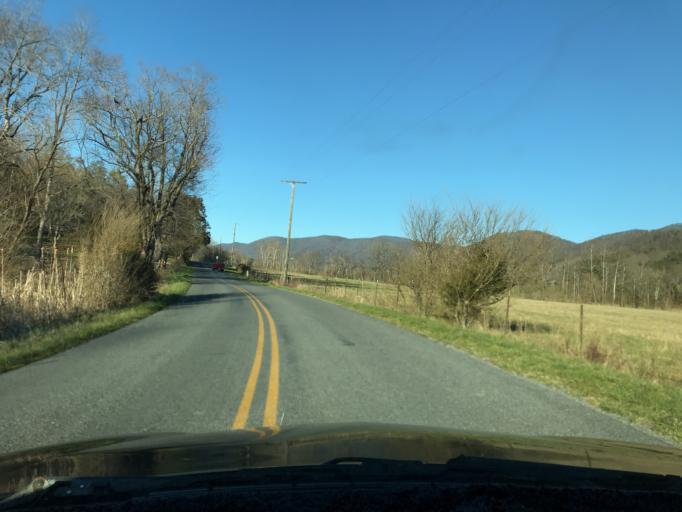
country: US
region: Virginia
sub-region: Botetourt County
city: Buchanan
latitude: 37.4175
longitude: -79.6976
